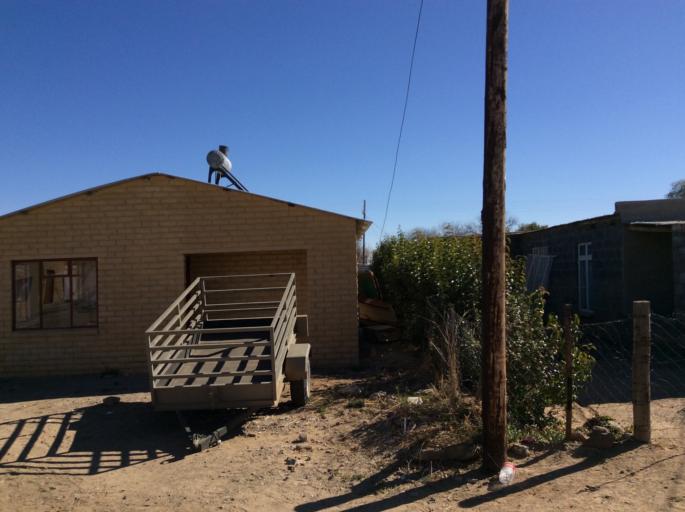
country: ZA
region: Orange Free State
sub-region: Lejweleputswa District Municipality
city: Brandfort
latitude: -28.7362
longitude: 26.1084
